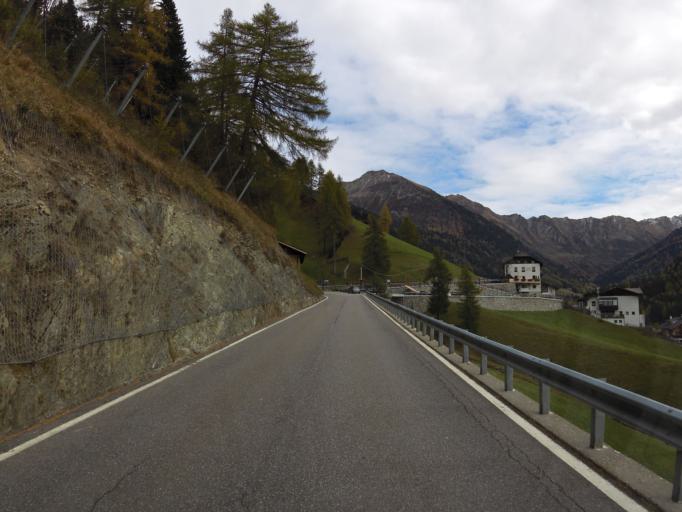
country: IT
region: Trentino-Alto Adige
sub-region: Bolzano
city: San Leonardo in Passiria
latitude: 46.8263
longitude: 11.2854
